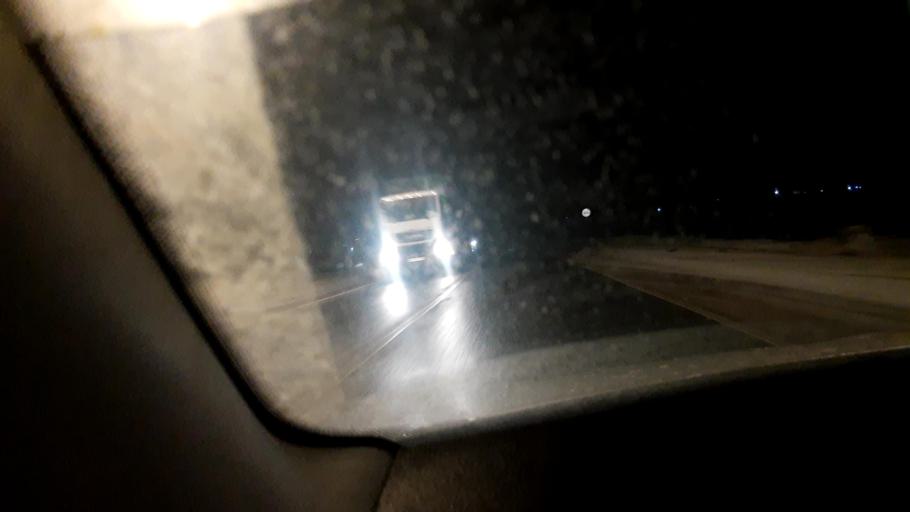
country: RU
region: Moskovskaya
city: Skoropuskovskiy
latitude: 56.4023
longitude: 38.1068
